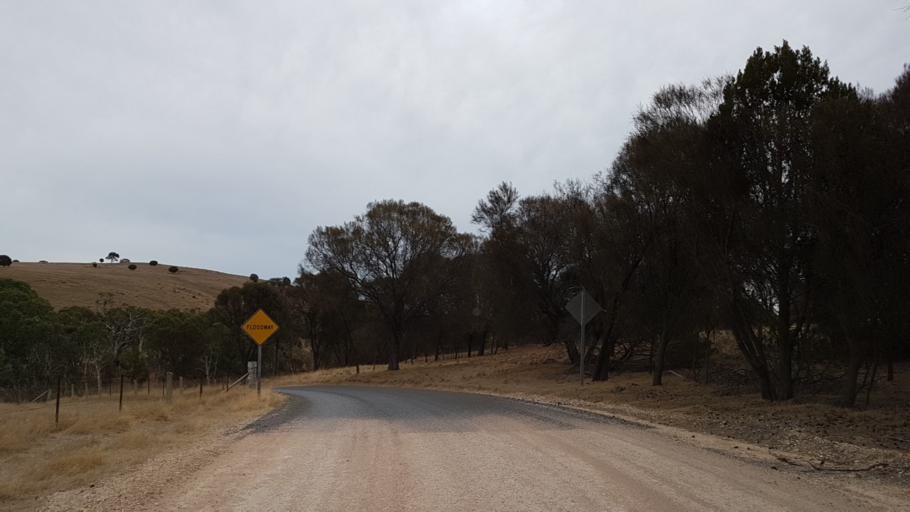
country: AU
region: South Australia
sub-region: Mount Barker
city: Callington
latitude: -35.0064
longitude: 139.0343
